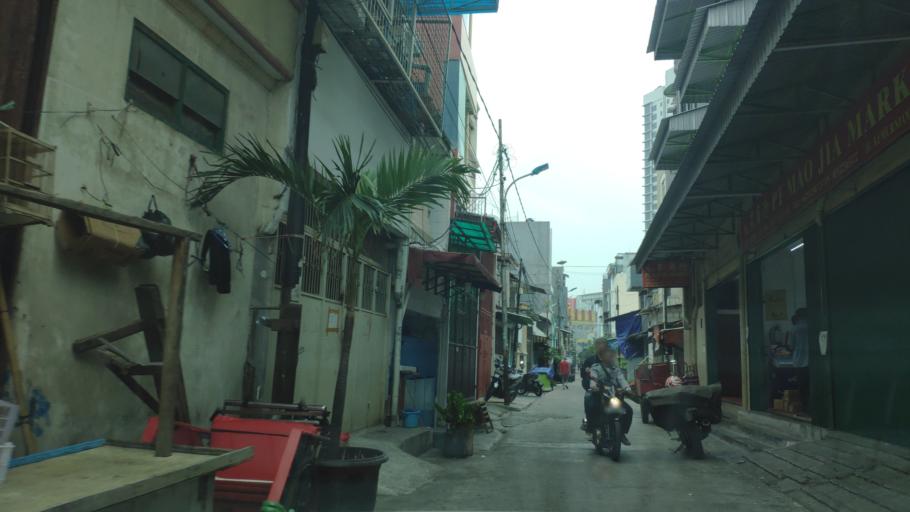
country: ID
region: Jakarta Raya
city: Jakarta
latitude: -6.1439
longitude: 106.8130
